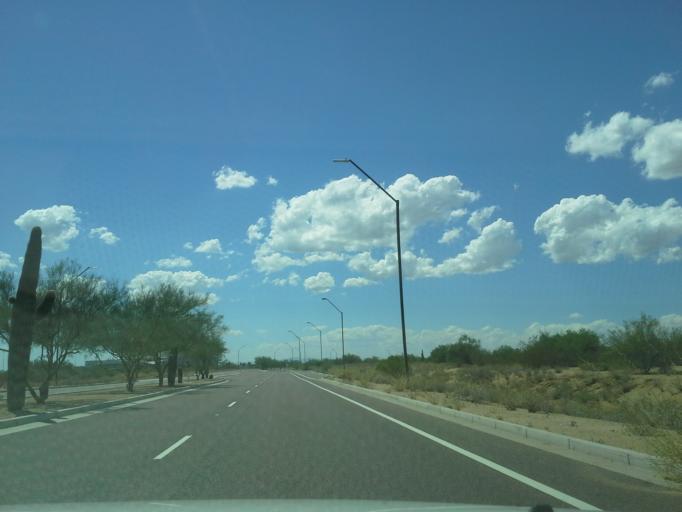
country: US
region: Arizona
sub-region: Maricopa County
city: Paradise Valley
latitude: 33.6623
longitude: -111.9140
